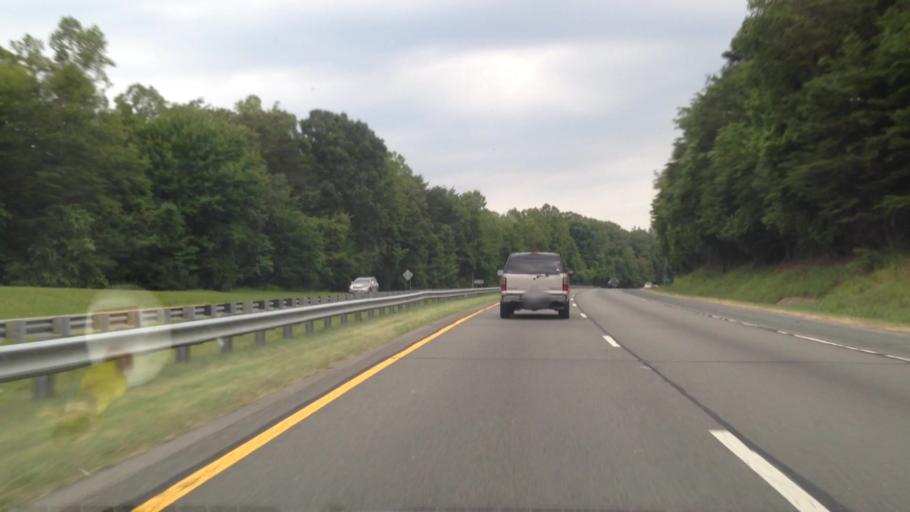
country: US
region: North Carolina
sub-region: Surry County
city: Pilot Mountain
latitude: 36.3241
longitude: -80.4483
